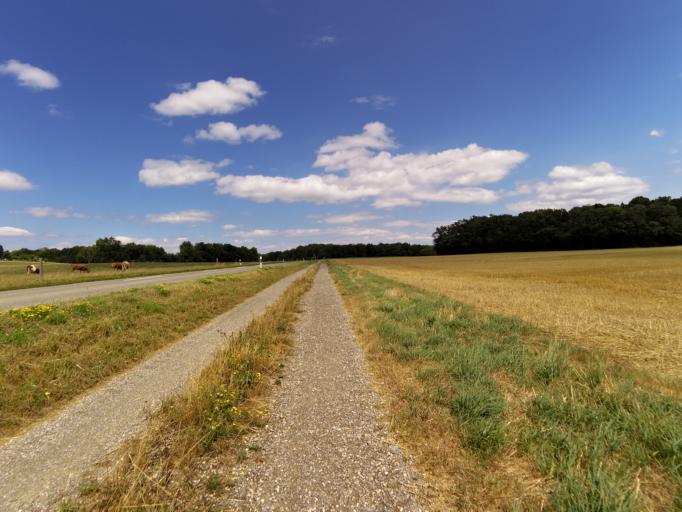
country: CH
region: Thurgau
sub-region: Kreuzlingen District
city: Tagerwilen
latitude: 47.6328
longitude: 9.0999
